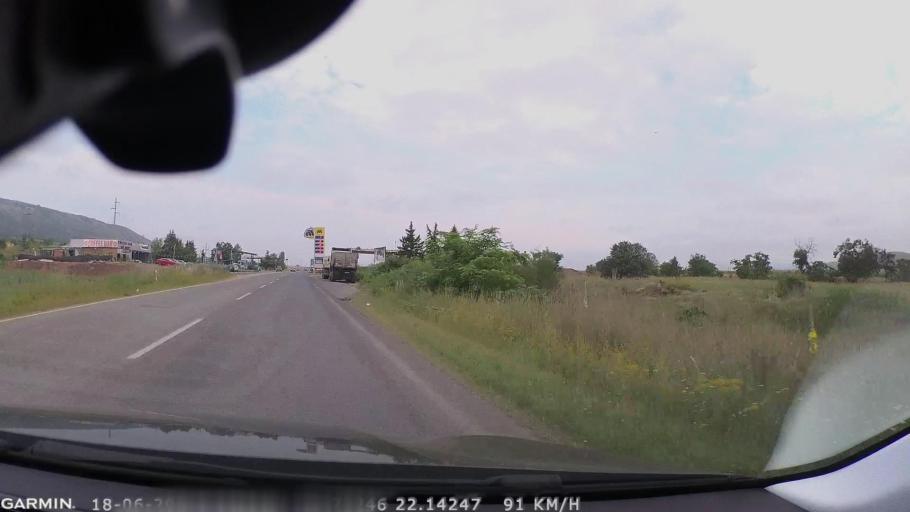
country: MK
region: Stip
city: Shtip
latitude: 41.7731
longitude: 22.1411
